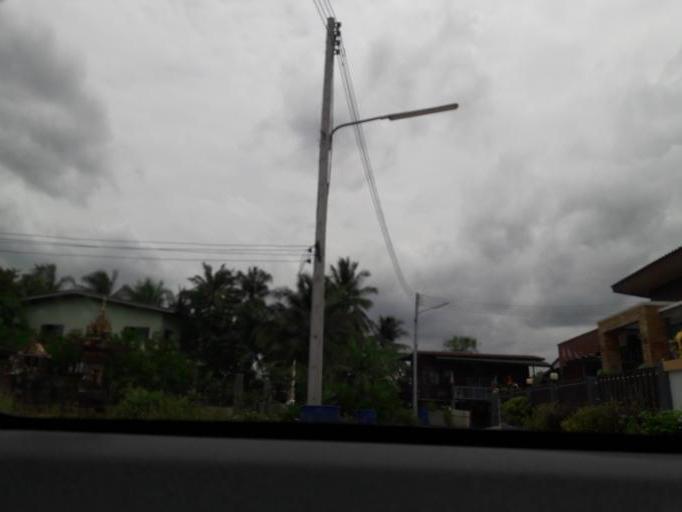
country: TH
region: Ratchaburi
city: Damnoen Saduak
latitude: 13.5747
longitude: 99.9916
